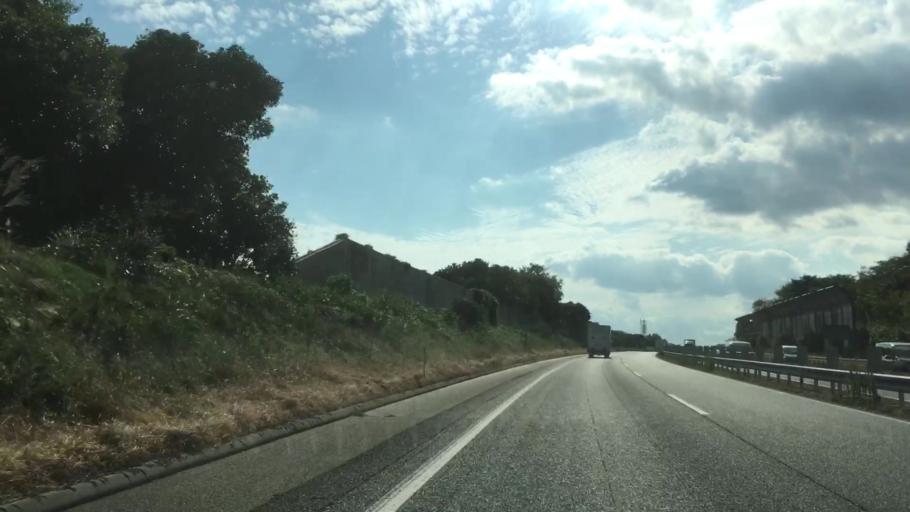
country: JP
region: Hiroshima
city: Ono-hara
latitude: 34.2767
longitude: 132.2551
